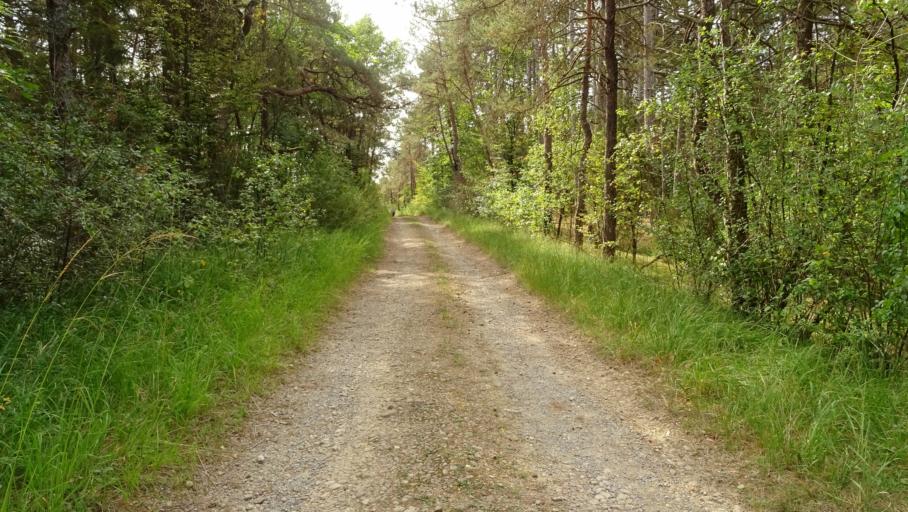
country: DE
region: Baden-Wuerttemberg
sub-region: Karlsruhe Region
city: Mosbach
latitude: 49.3891
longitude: 9.1583
